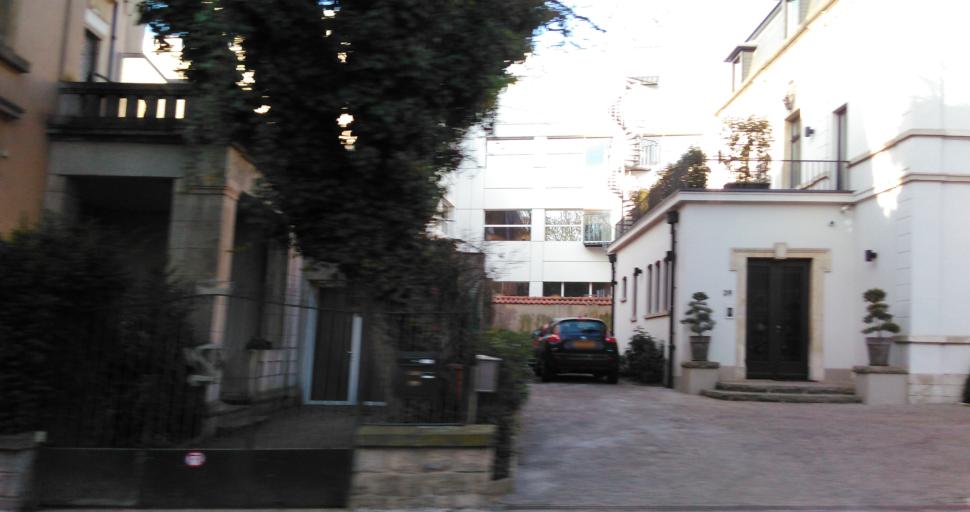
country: LU
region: Luxembourg
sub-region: Canton de Luxembourg
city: Luxembourg
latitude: 49.6133
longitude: 6.1211
